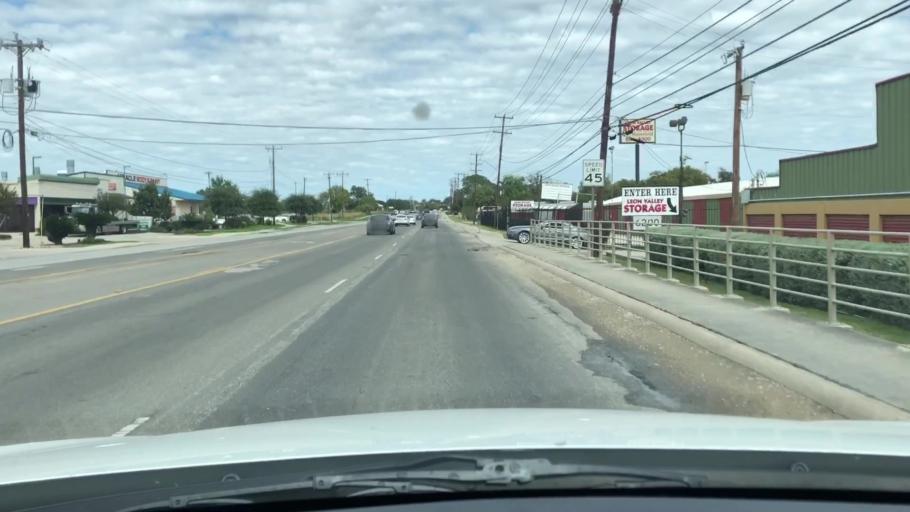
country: US
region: Texas
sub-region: Bexar County
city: Leon Valley
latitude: 29.4901
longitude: -98.6222
